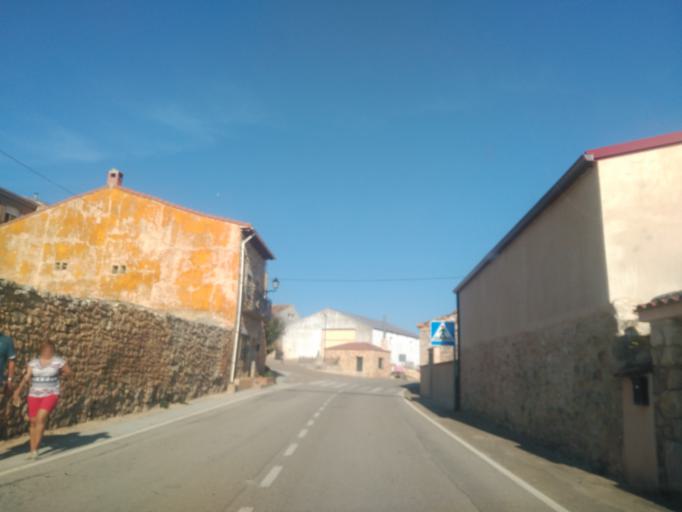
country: ES
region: Castille and Leon
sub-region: Provincia de Burgos
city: Brazacorta
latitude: 41.7197
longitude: -3.3427
